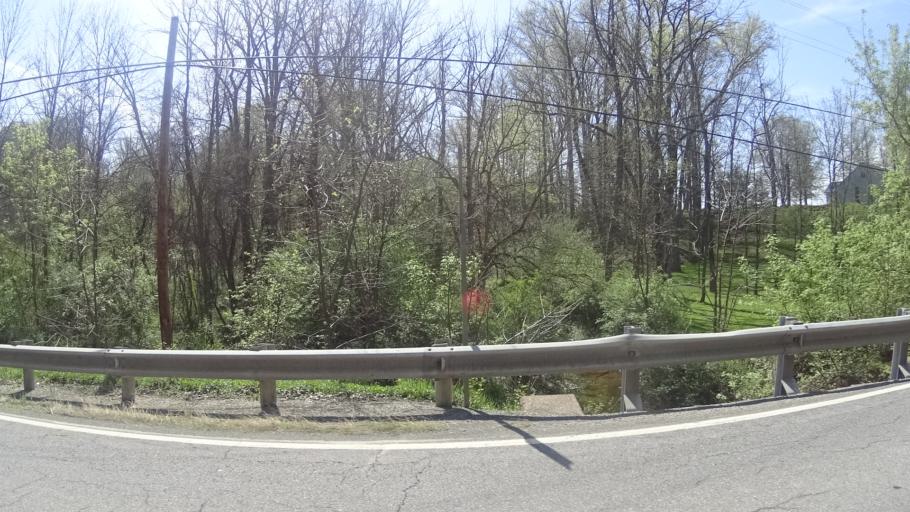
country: US
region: Ohio
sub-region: Lorain County
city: Lagrange
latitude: 41.3016
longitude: -82.1309
